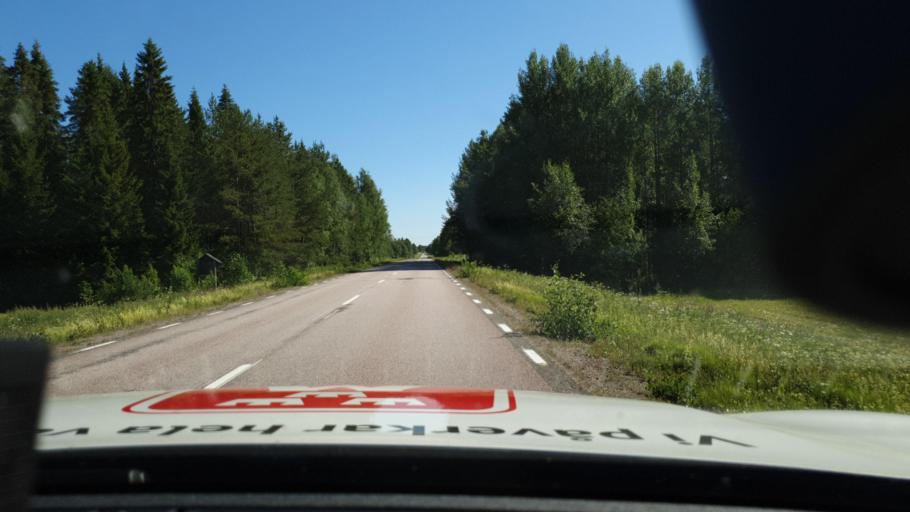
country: SE
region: Norrbotten
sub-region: Lulea Kommun
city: Ranea
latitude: 65.9134
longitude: 22.4506
